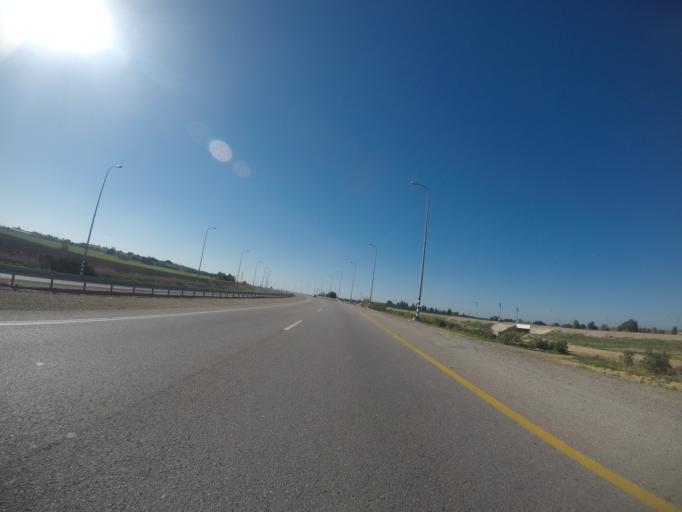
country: IL
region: Southern District
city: Ashdod
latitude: 31.7496
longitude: 34.6509
